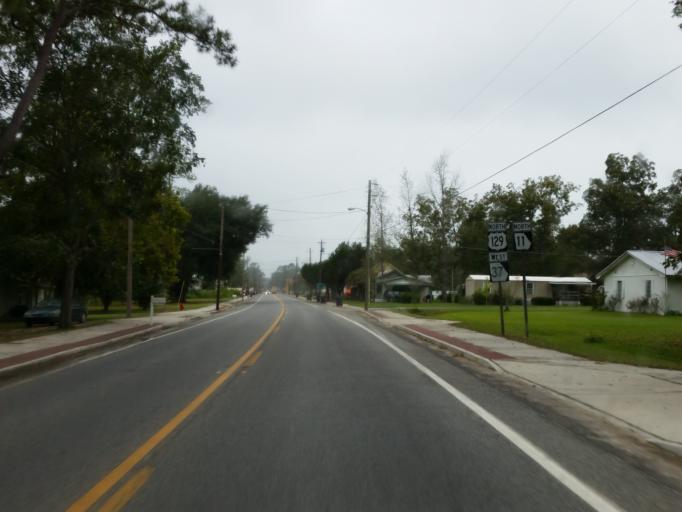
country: US
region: Georgia
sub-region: Berrien County
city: Ray City
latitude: 31.0757
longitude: -83.1932
